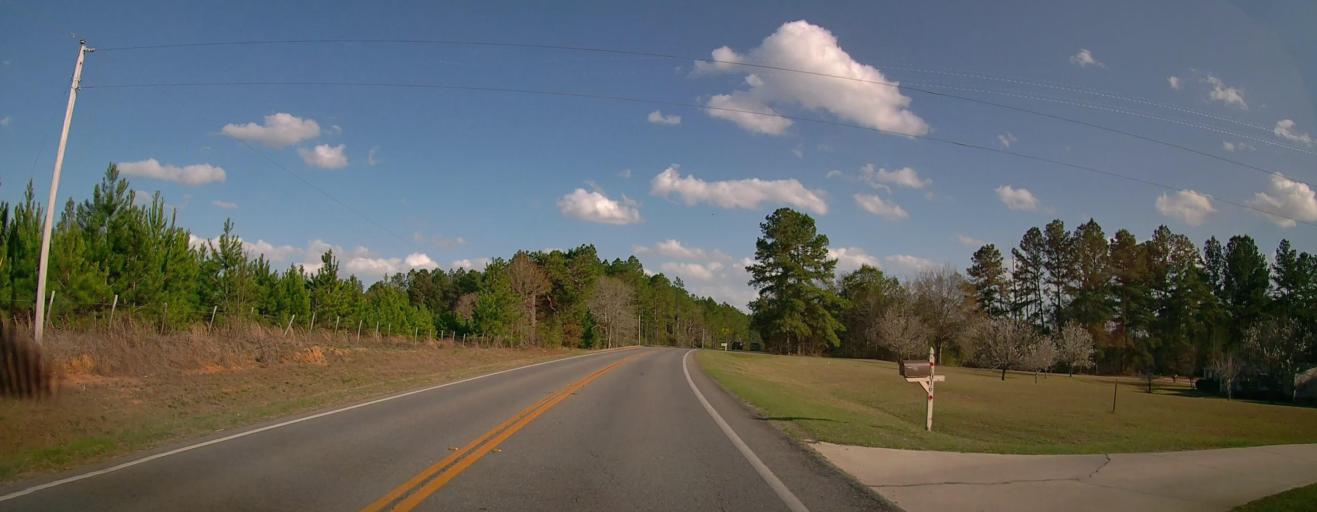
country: US
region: Georgia
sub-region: Toombs County
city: Lyons
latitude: 32.1732
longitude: -82.2773
